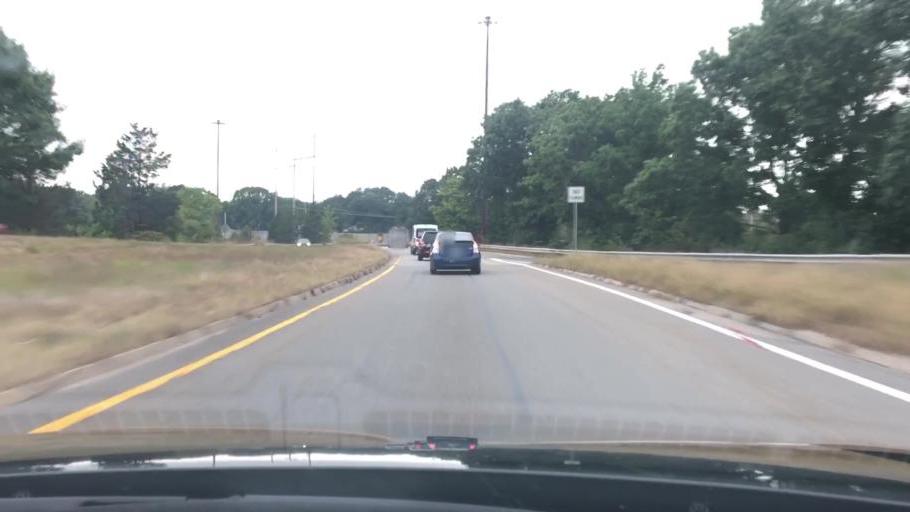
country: US
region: Massachusetts
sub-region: Middlesex County
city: Lowell
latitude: 42.6085
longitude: -71.3232
